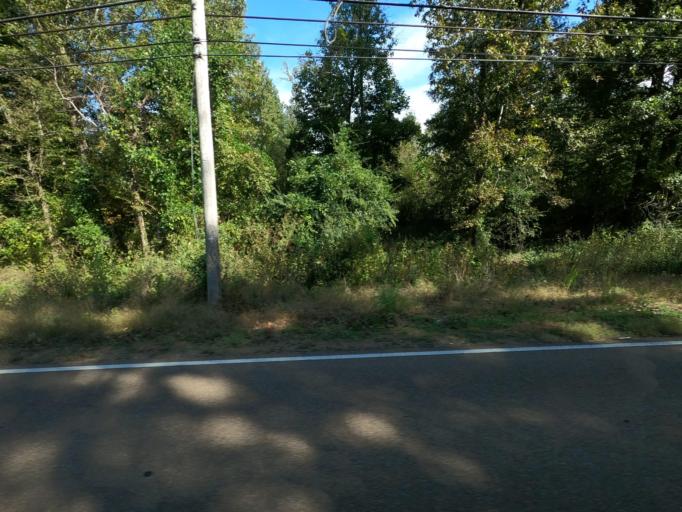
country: US
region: Tennessee
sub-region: Fayette County
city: Hickory Withe
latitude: 35.2242
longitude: -89.6503
